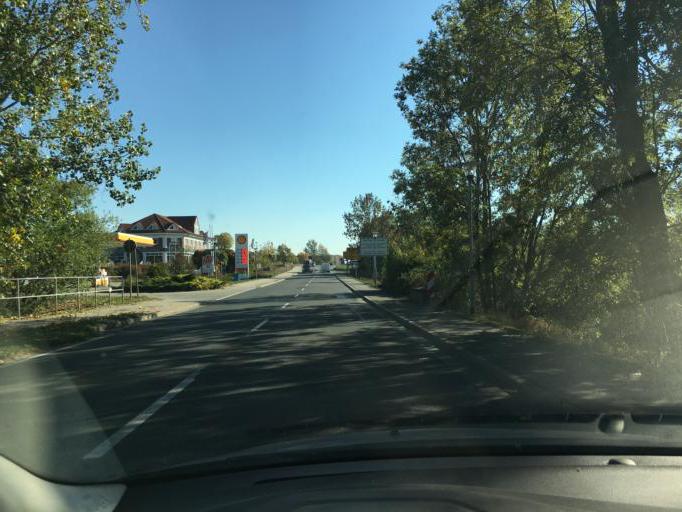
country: DE
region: Saxony-Anhalt
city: Wanzleben
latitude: 52.0560
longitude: 11.4492
